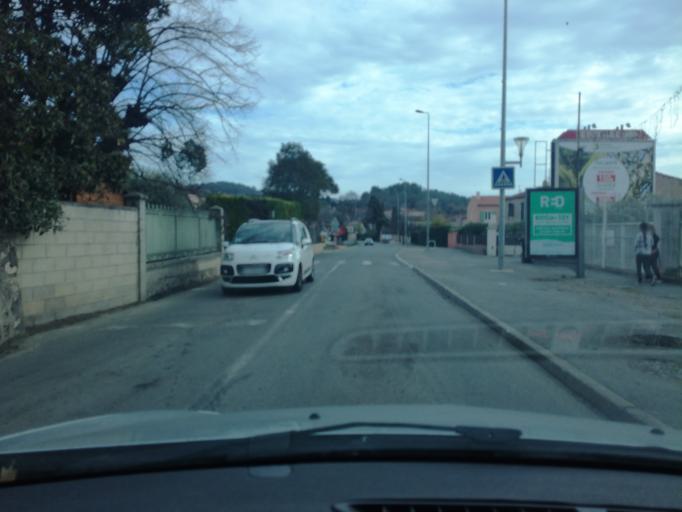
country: FR
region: Provence-Alpes-Cote d'Azur
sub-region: Departement des Alpes-Maritimes
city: Mouans-Sartoux
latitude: 43.6440
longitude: 6.9548
